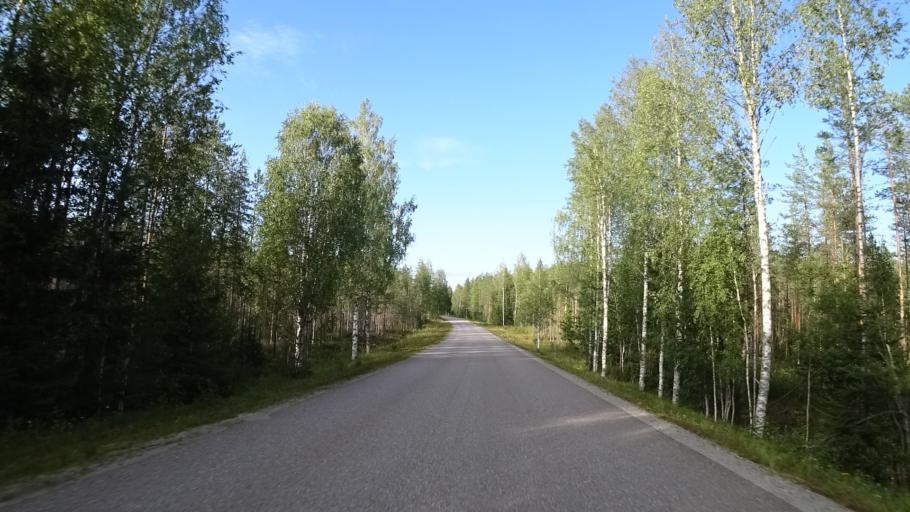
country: FI
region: North Karelia
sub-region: Joensuu
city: Eno
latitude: 63.0166
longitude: 30.4914
